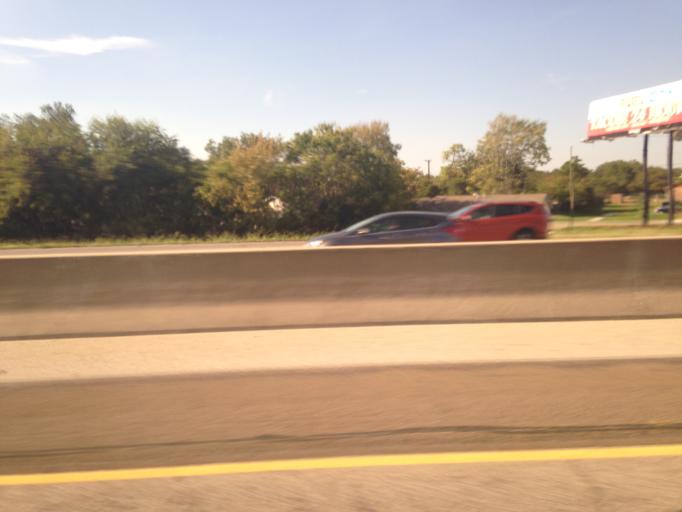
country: US
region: Texas
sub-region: Tarrant County
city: Haltom City
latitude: 32.7801
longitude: -97.2765
